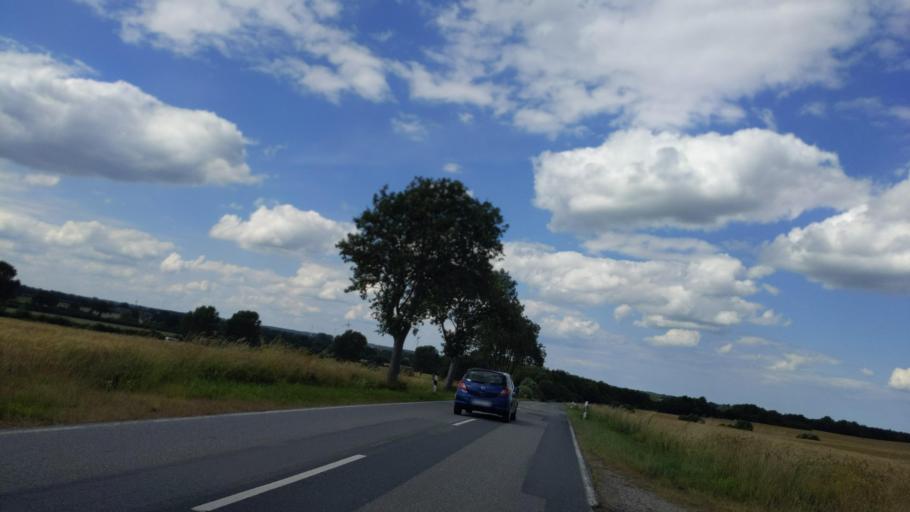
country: DE
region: Schleswig-Holstein
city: Altenkrempe
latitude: 54.1403
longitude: 10.8473
